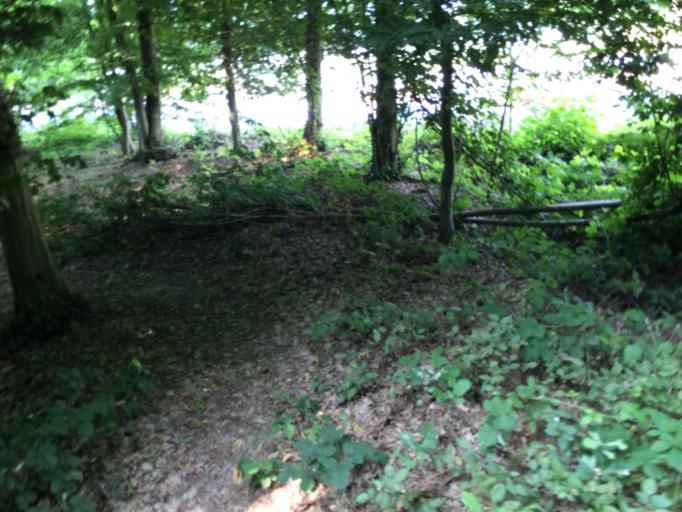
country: FR
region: Ile-de-France
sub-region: Departement des Hauts-de-Seine
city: Chatenay-Malabry
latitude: 48.7709
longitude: 2.2432
